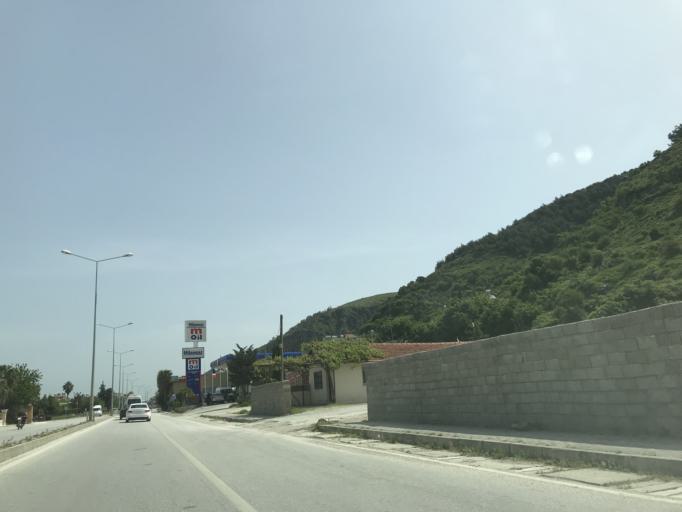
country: TR
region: Hatay
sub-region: Antakya Ilcesi
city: Antakya
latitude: 36.2156
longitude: 36.1804
